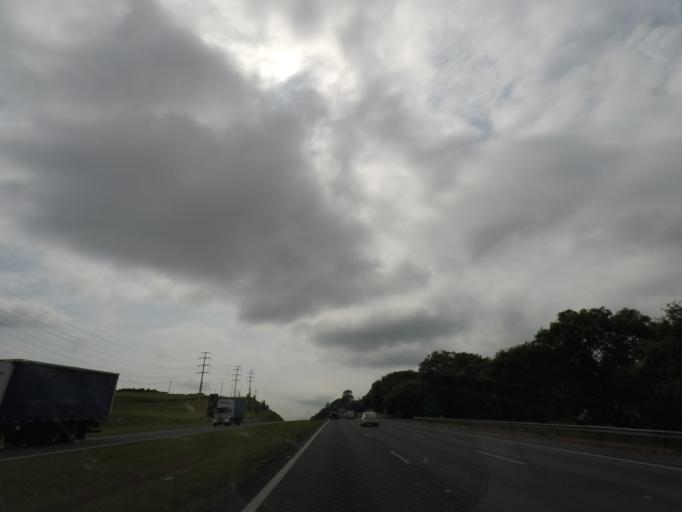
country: BR
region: Sao Paulo
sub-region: Campinas
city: Campinas
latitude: -22.8994
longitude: -46.9993
